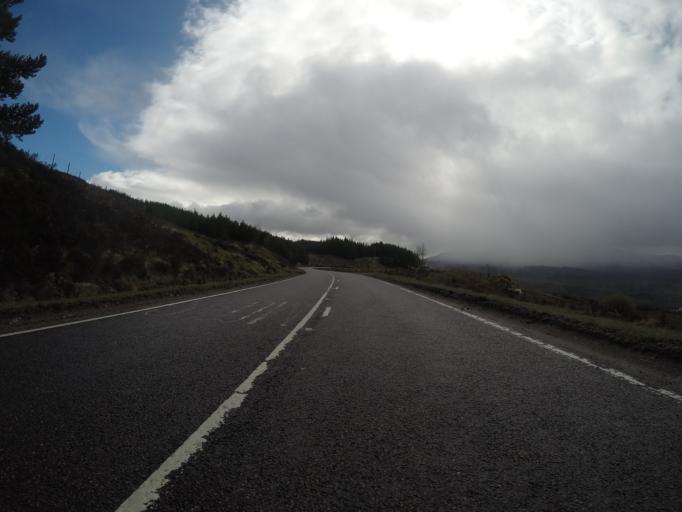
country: GB
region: Scotland
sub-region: Highland
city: Spean Bridge
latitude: 57.0869
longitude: -4.9648
